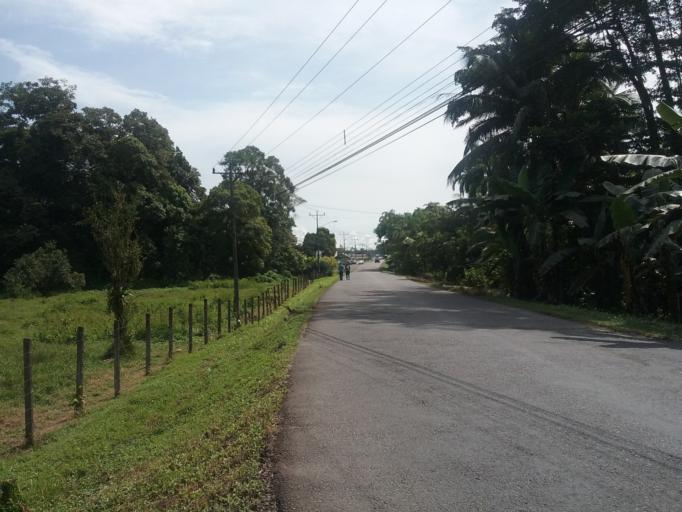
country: CR
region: Limon
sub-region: Canton de Pococi
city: Guapiles
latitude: 10.3203
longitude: -83.9088
